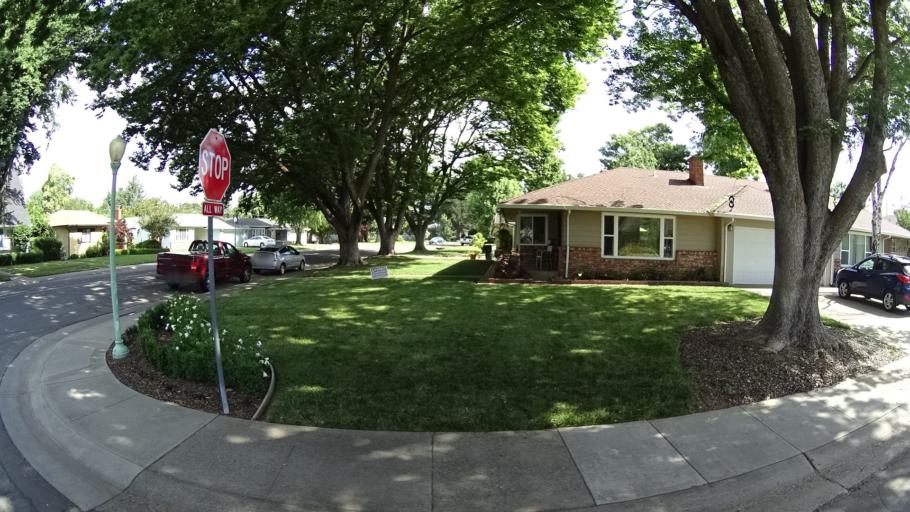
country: US
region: California
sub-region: Sacramento County
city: Sacramento
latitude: 38.5784
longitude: -121.4340
